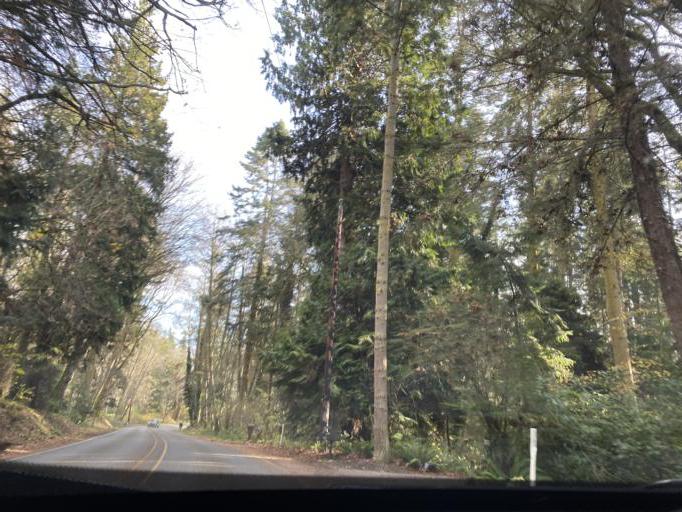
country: US
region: Washington
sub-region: Island County
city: Langley
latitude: 47.9713
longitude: -122.4506
